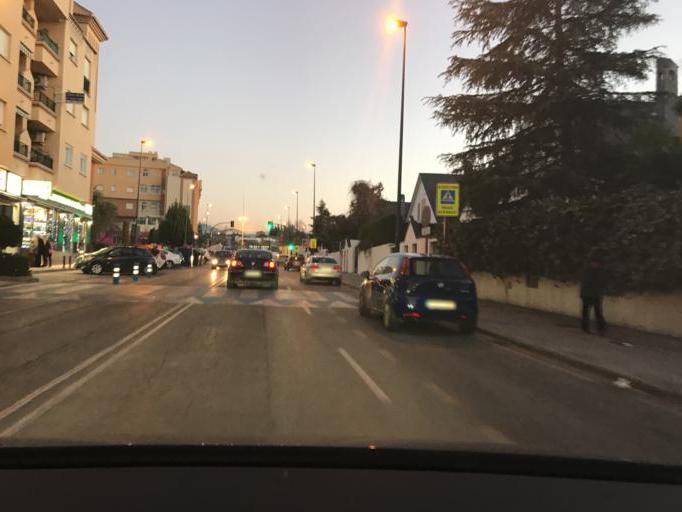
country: ES
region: Andalusia
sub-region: Provincia de Granada
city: Ogijares
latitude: 37.1190
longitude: -3.6046
